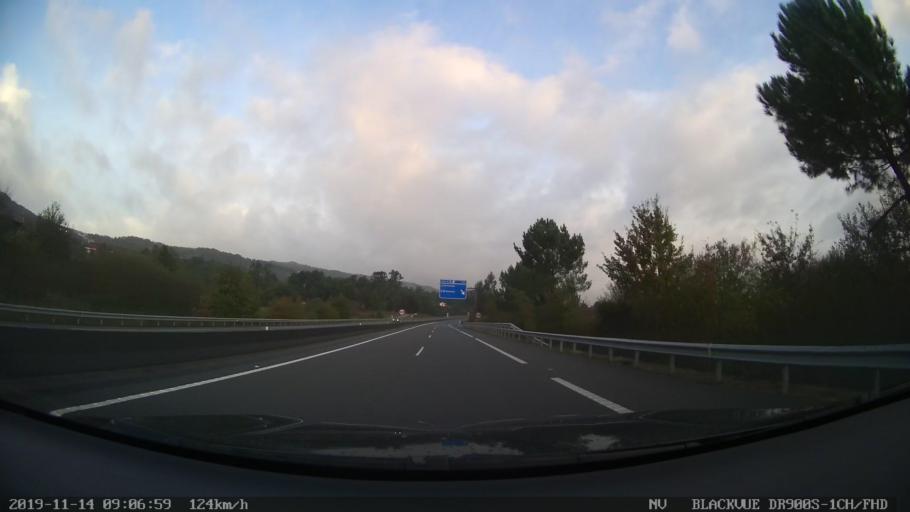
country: ES
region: Galicia
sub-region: Provincia de Pontevedra
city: Porrino
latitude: 42.1362
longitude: -8.6371
